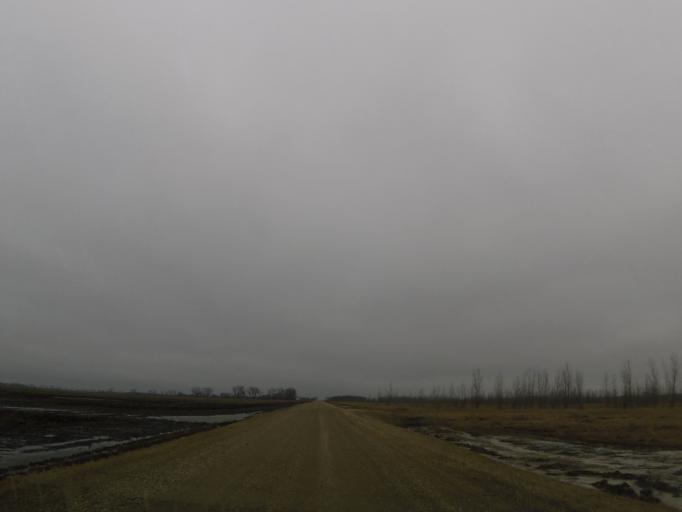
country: US
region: North Dakota
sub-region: Walsh County
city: Grafton
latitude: 48.3764
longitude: -97.1677
